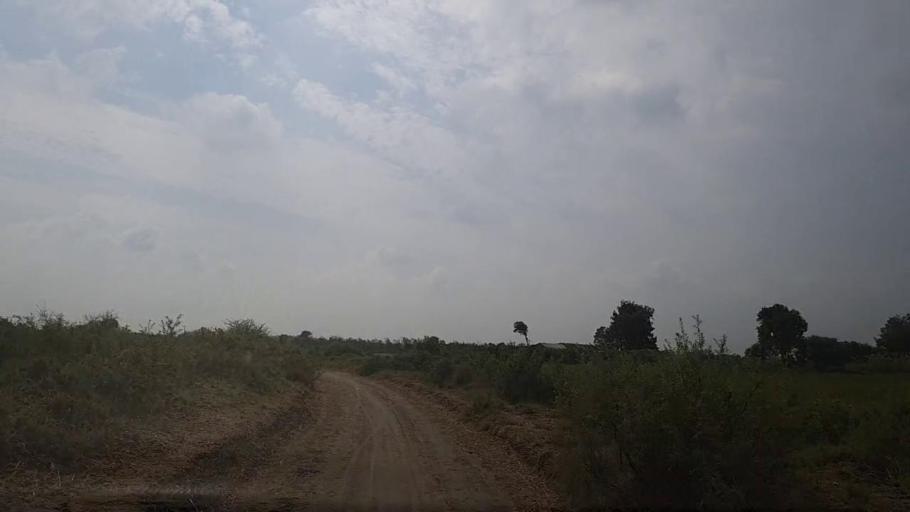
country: PK
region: Sindh
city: Mirpur Batoro
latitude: 24.6054
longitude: 68.1396
